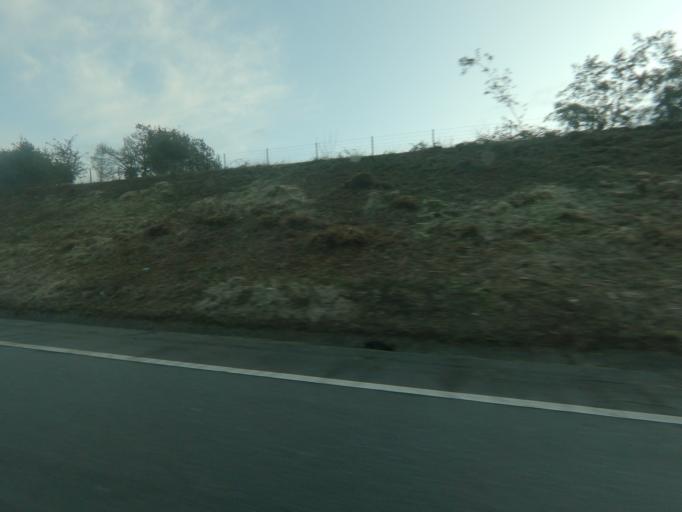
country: PT
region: Viana do Castelo
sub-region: Valenca
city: Valenca
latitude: 42.0244
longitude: -8.6498
